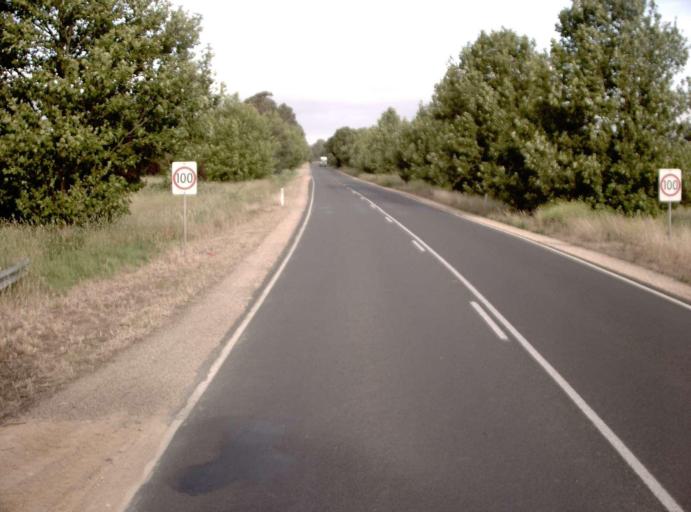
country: AU
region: Victoria
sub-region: Wellington
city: Heyfield
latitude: -37.9652
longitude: 146.9022
